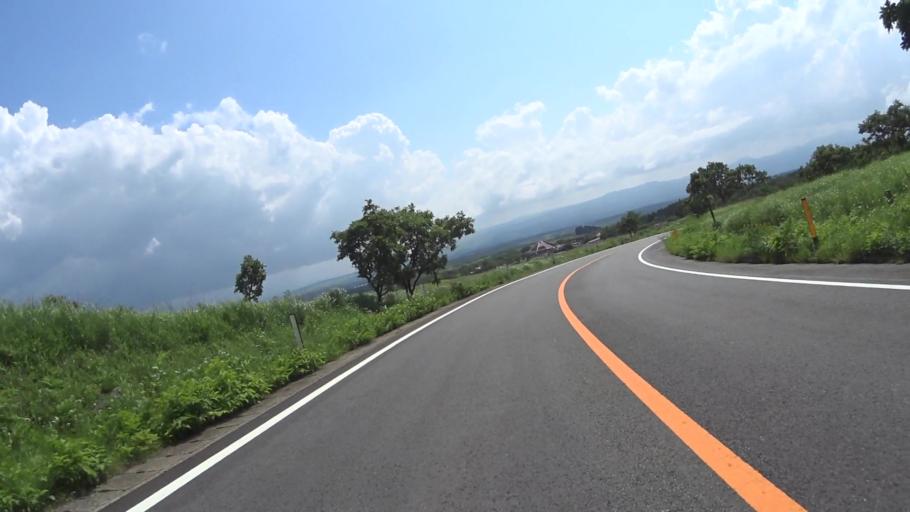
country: JP
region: Kumamoto
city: Aso
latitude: 33.0741
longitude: 131.1947
